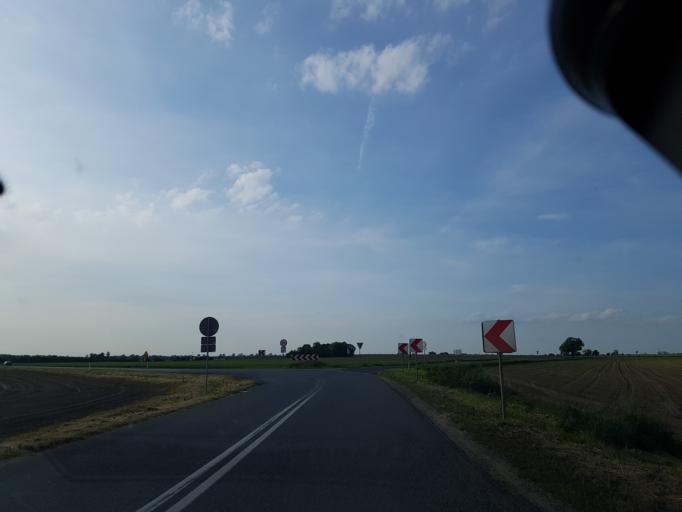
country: PL
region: Lower Silesian Voivodeship
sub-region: Powiat wroclawski
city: Kobierzyce
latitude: 50.9359
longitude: 16.9379
